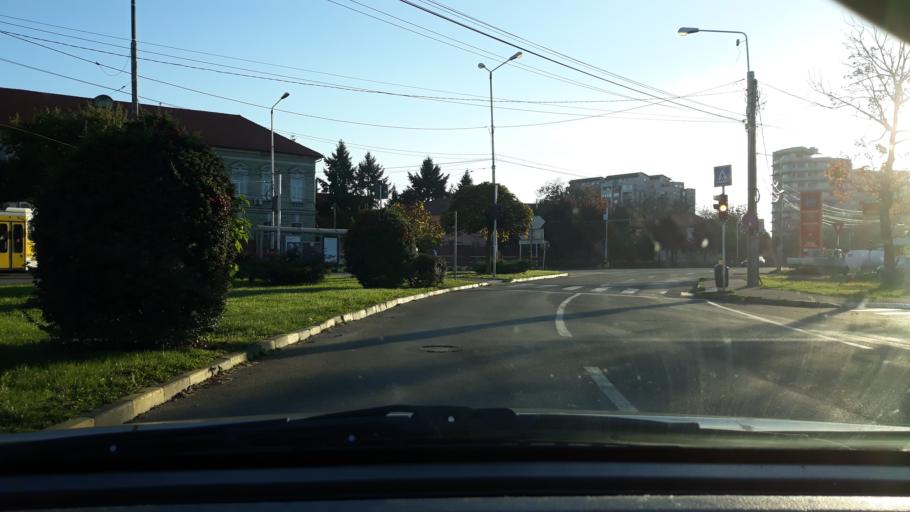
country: RO
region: Bihor
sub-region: Comuna Biharea
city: Oradea
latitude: 47.0561
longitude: 21.9169
